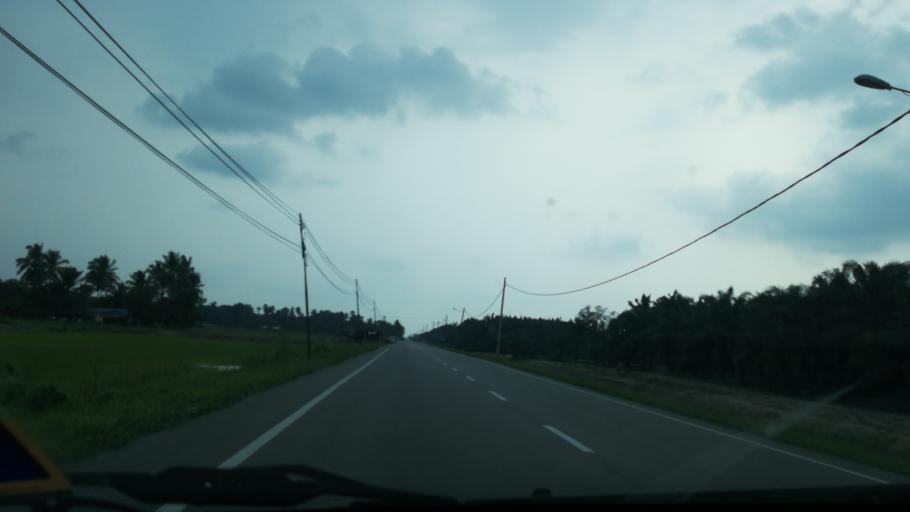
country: MY
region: Perak
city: Teluk Intan
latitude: 4.1182
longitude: 101.0761
